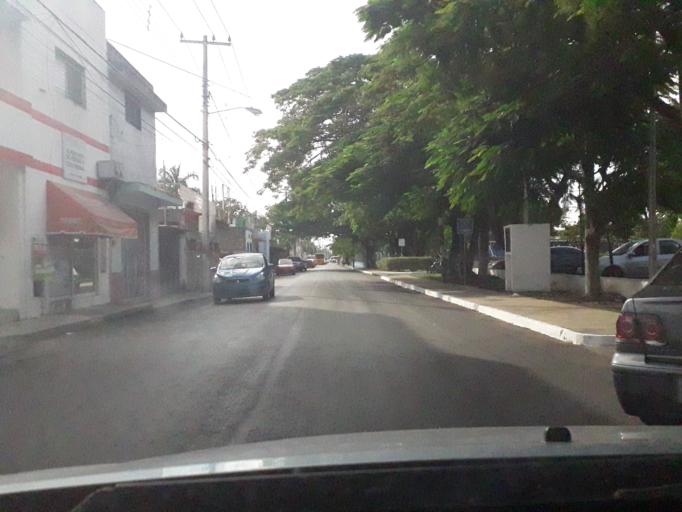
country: MX
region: Yucatan
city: Merida
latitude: 21.0119
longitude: -89.6325
